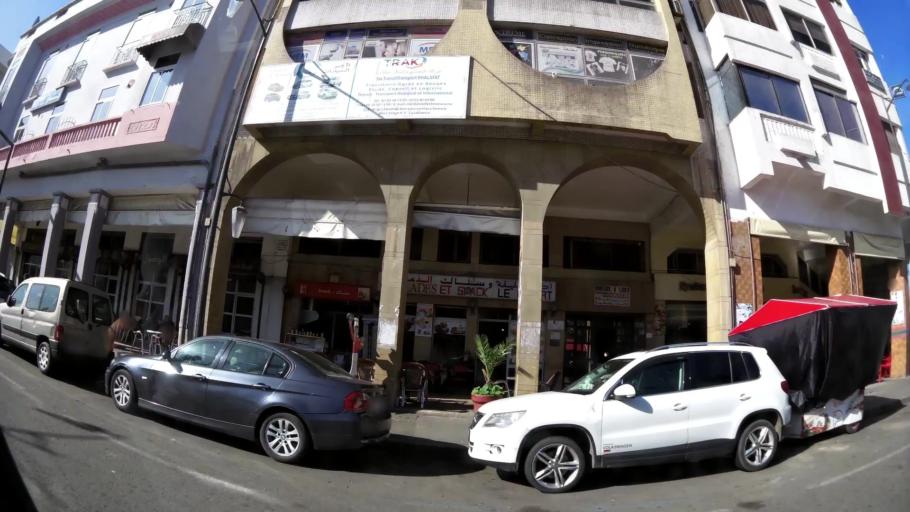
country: MA
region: Grand Casablanca
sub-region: Casablanca
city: Casablanca
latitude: 33.5897
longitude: -7.5923
